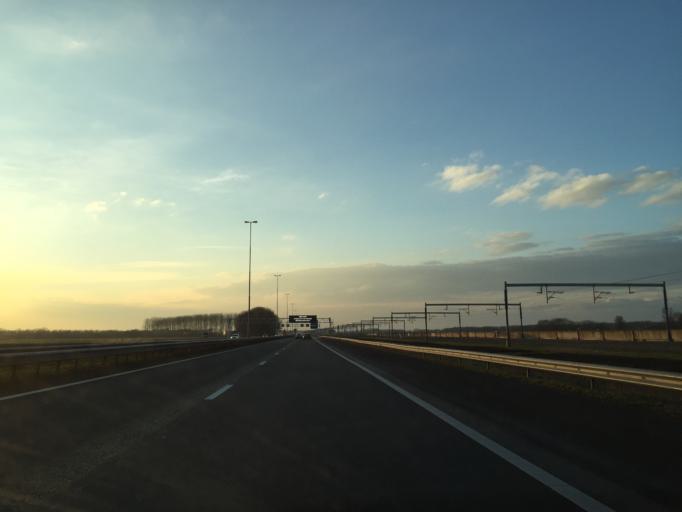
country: NL
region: North Brabant
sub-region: Gemeente Woudrichem
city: Woudrichem
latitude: 51.8406
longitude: 5.0349
